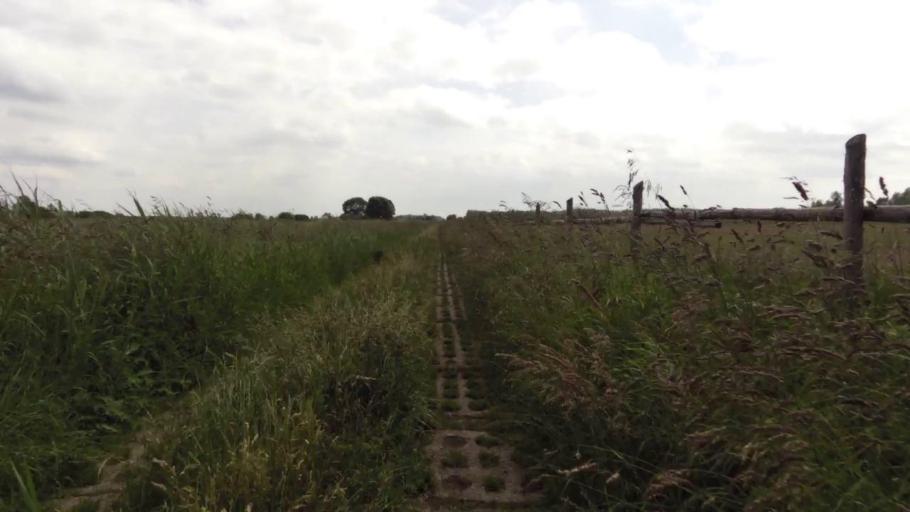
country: PL
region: West Pomeranian Voivodeship
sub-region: Powiat goleniowski
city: Stepnica
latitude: 53.7185
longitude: 14.6080
